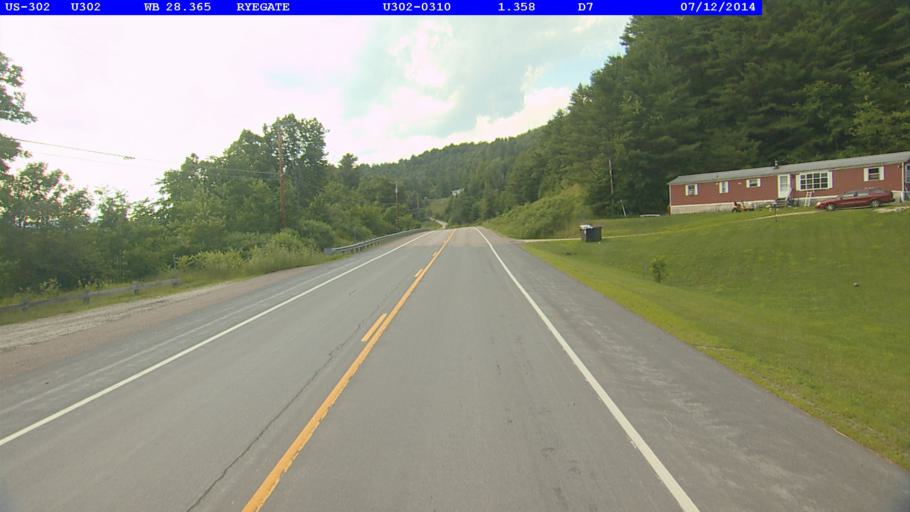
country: US
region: New Hampshire
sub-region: Grafton County
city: Woodsville
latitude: 44.1946
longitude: -72.1492
